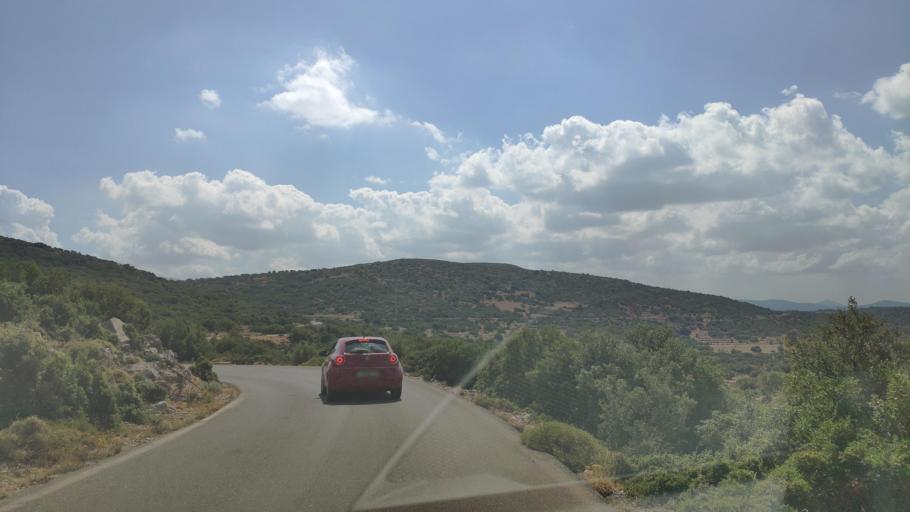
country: GR
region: Peloponnese
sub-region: Nomos Lakonias
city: Kariai
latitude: 37.3019
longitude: 22.4604
